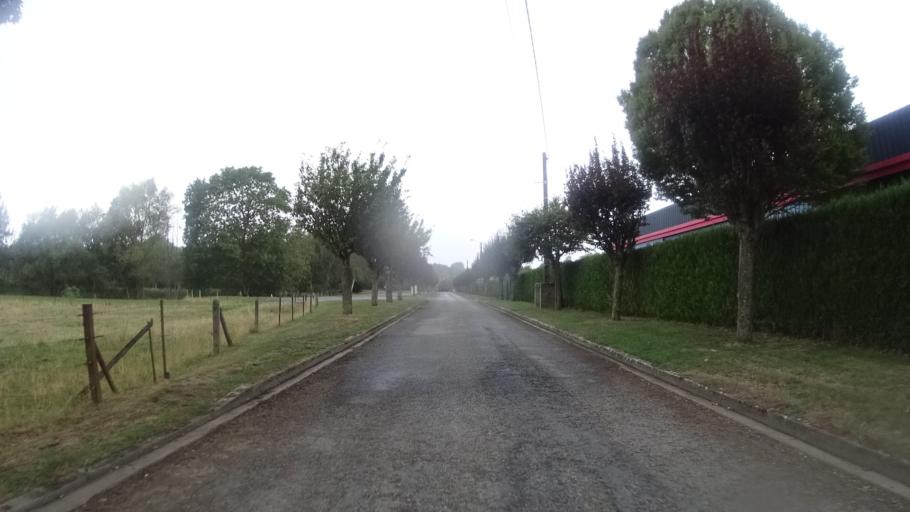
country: FR
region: Picardie
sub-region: Departement de l'Aisne
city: Ribemont
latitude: 49.8259
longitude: 3.4683
